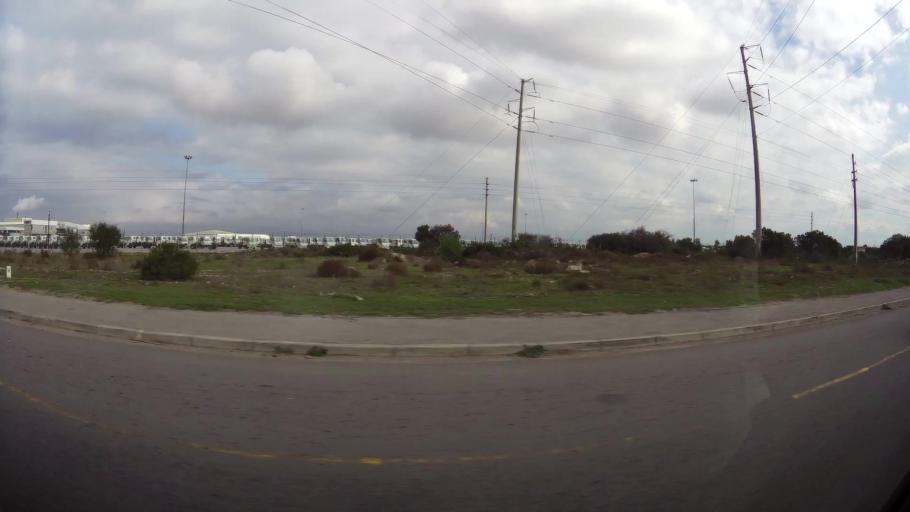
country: ZA
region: Eastern Cape
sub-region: Nelson Mandela Bay Metropolitan Municipality
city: Port Elizabeth
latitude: -33.8090
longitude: 25.6263
